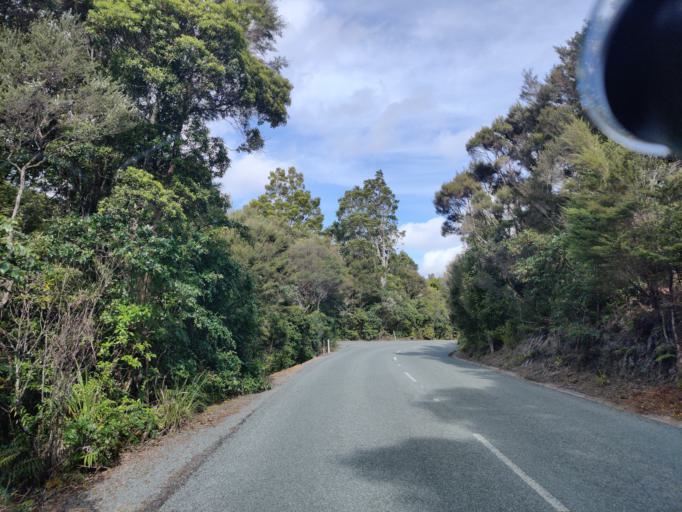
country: NZ
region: Northland
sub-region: Far North District
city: Waimate North
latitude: -35.6098
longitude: 173.5420
